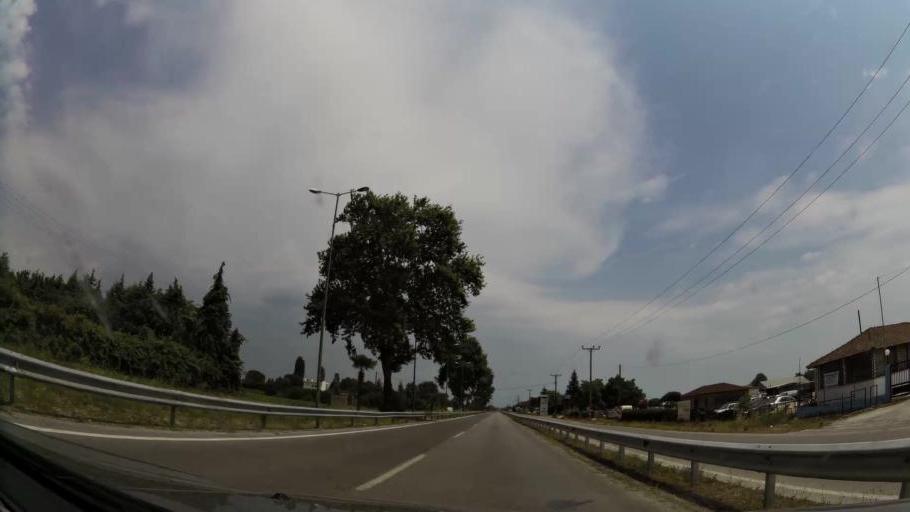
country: GR
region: Central Macedonia
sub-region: Nomos Pierias
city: Peristasi
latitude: 40.2721
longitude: 22.5589
